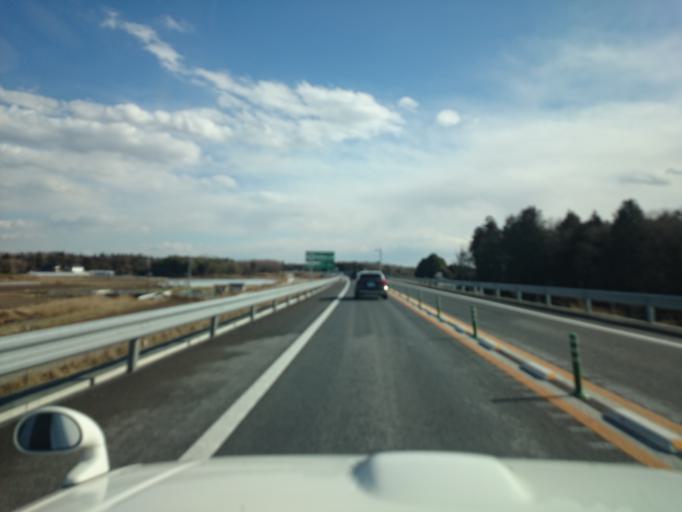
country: JP
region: Ibaraki
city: Iwai
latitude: 36.0963
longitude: 139.8706
